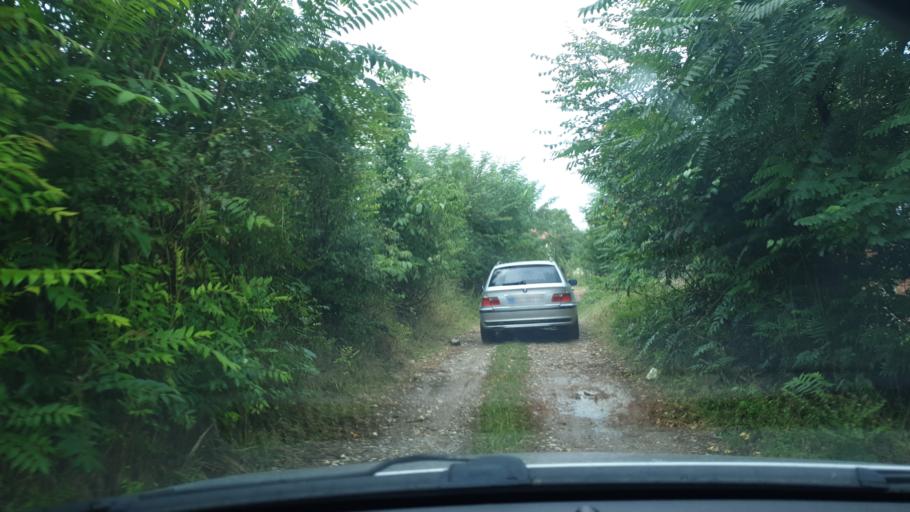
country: RS
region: Central Serbia
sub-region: Sumadijski Okrug
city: Kragujevac
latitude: 44.0795
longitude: 20.7989
